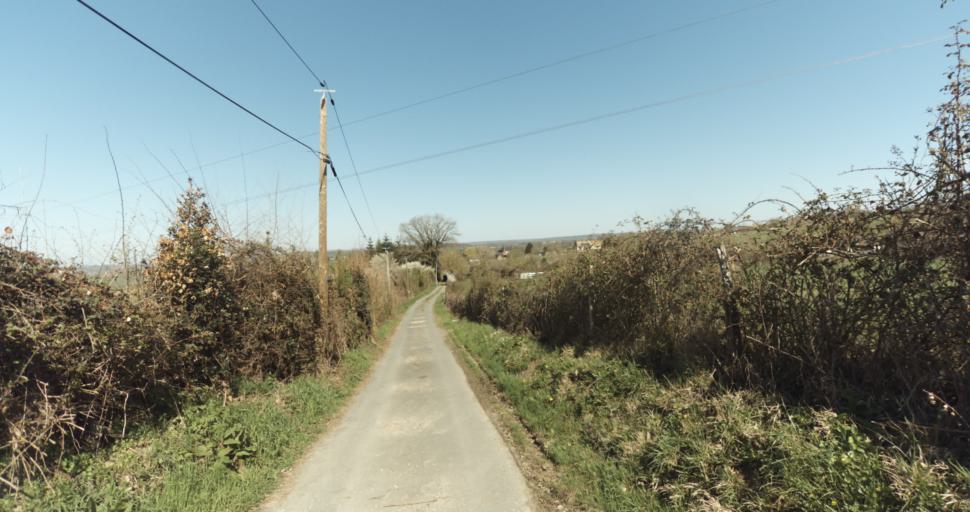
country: FR
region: Lower Normandy
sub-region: Departement du Calvados
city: Saint-Pierre-sur-Dives
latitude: 49.0149
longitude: 0.0443
